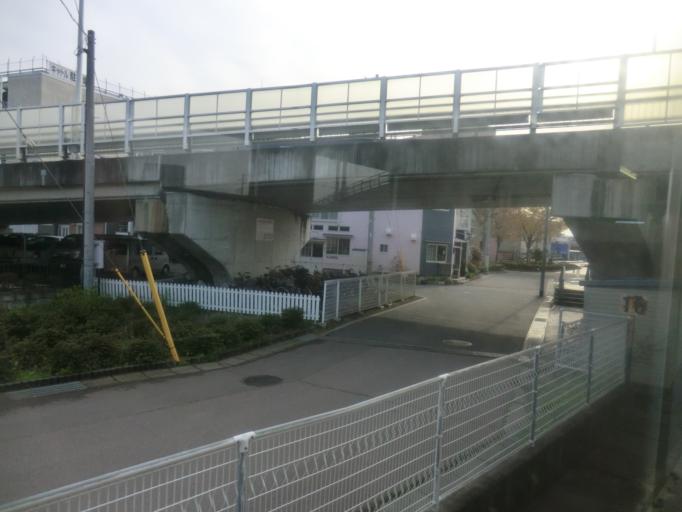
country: JP
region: Iwate
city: Miyako
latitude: 39.6406
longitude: 141.9449
